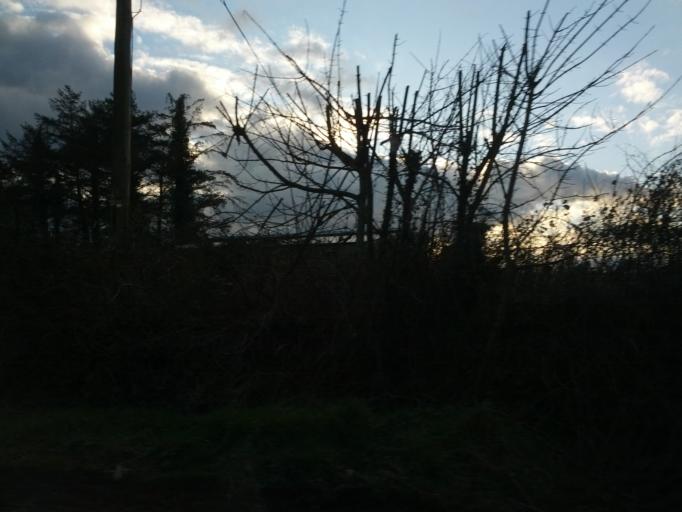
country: IE
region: Connaught
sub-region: County Galway
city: Athenry
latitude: 53.4183
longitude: -8.6881
